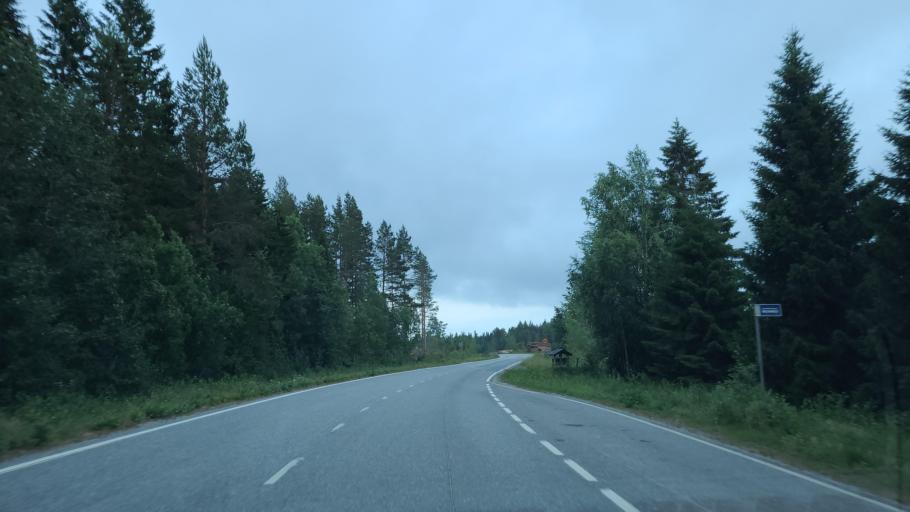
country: FI
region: Ostrobothnia
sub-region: Vaasa
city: Replot
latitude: 63.2794
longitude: 21.1336
